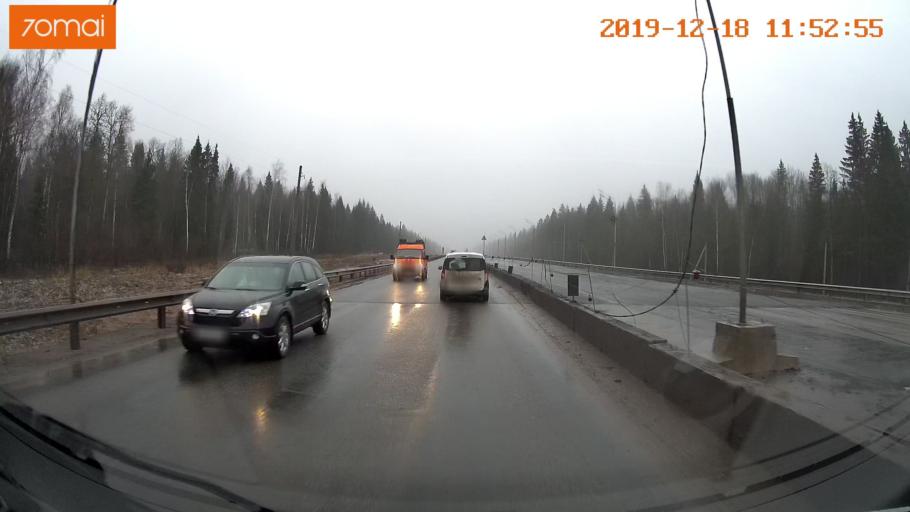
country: RU
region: Moskovskaya
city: Yershovo
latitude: 55.7992
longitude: 36.9208
